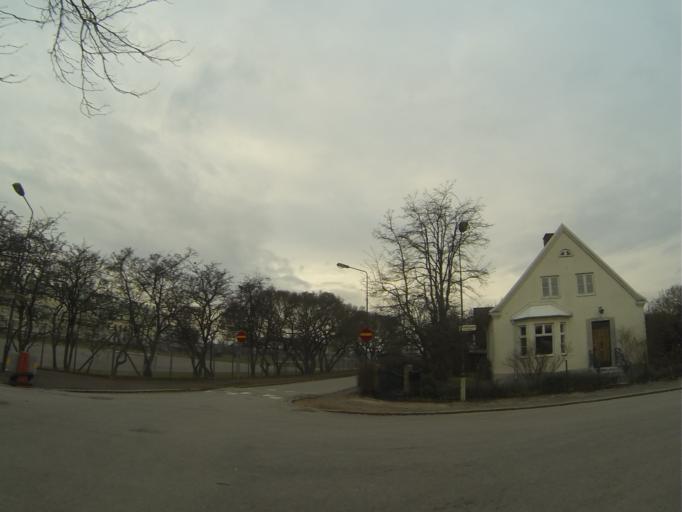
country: SE
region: Skane
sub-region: Burlovs Kommun
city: Arloev
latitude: 55.6117
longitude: 13.0431
